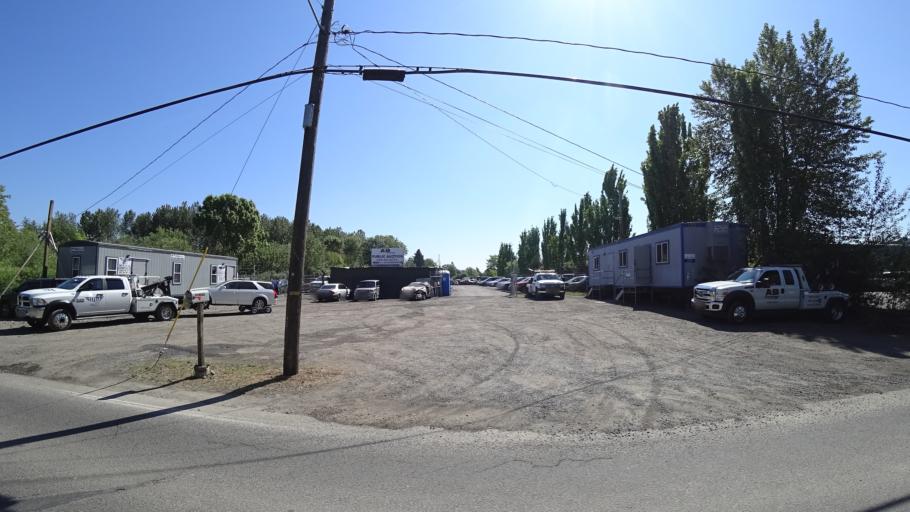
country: US
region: Oregon
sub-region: Multnomah County
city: Lents
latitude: 45.4799
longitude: -122.5490
